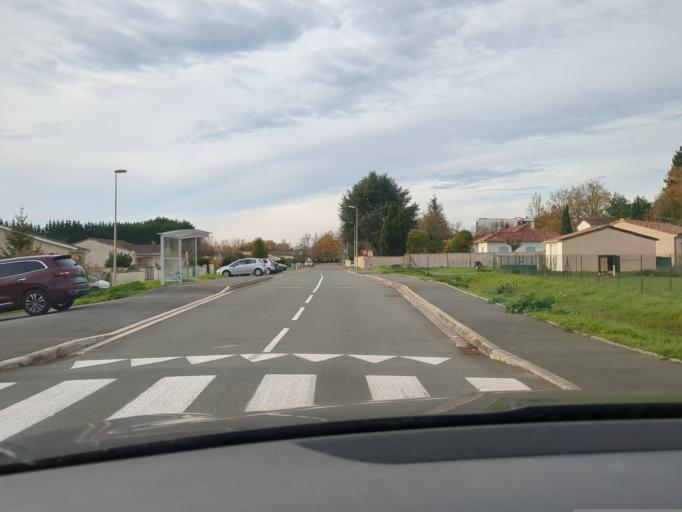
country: FR
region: Poitou-Charentes
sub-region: Departement de la Charente-Maritime
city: Jonzac
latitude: 45.4526
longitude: -0.4453
